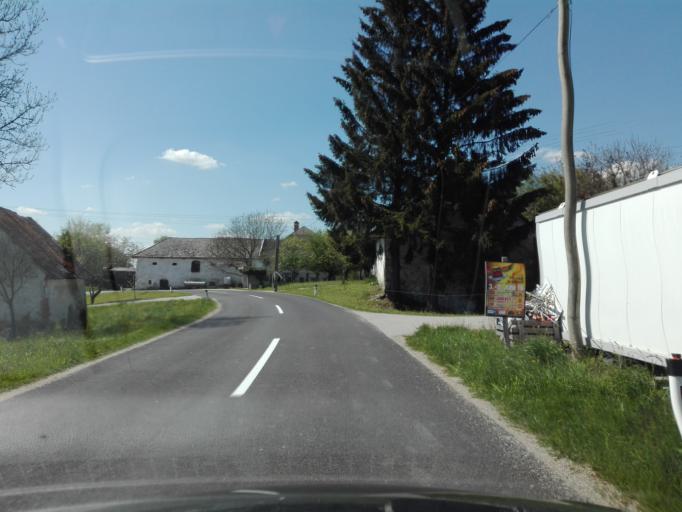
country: AT
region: Upper Austria
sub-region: Politischer Bezirk Rohrbach
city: Kleinzell im Muehlkreis
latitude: 48.3671
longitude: 13.9263
